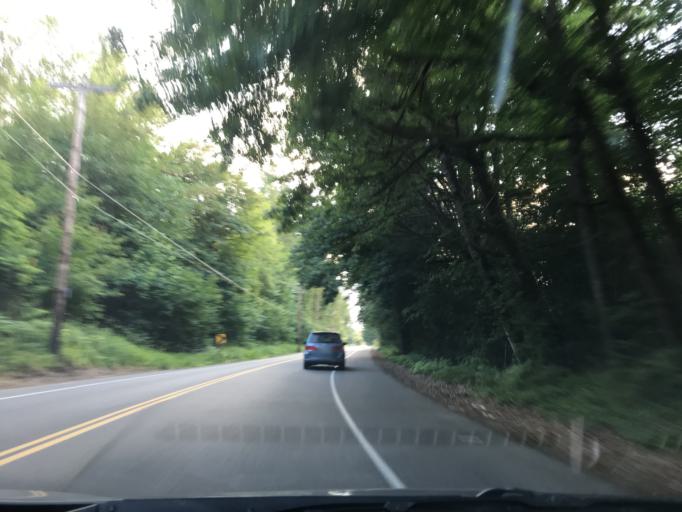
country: US
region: Washington
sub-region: King County
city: Black Diamond
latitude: 47.2976
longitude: -122.0585
